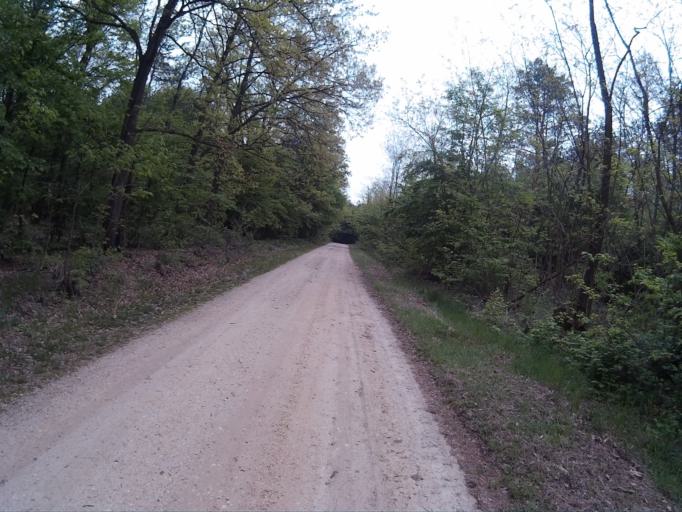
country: HU
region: Vas
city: Vasvar
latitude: 47.0660
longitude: 16.8697
